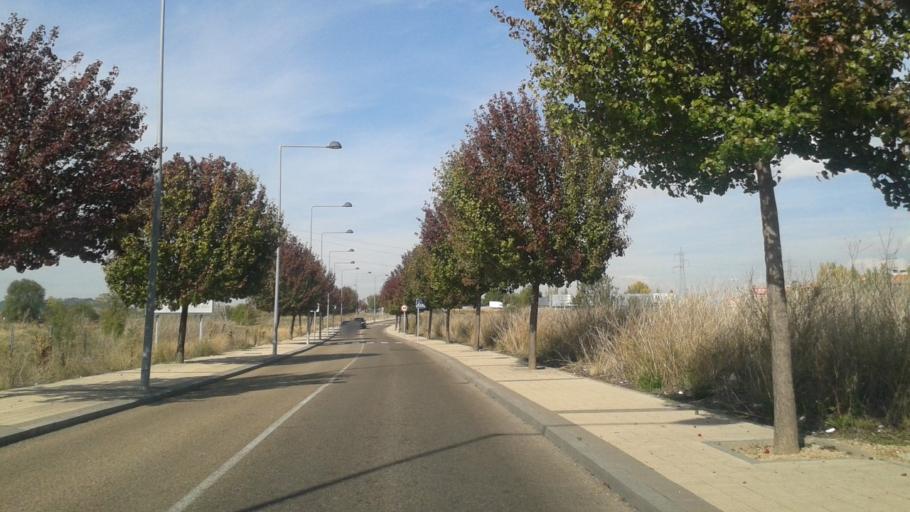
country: ES
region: Castille and Leon
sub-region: Provincia de Valladolid
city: Zaratan
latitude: 41.6315
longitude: -4.7729
